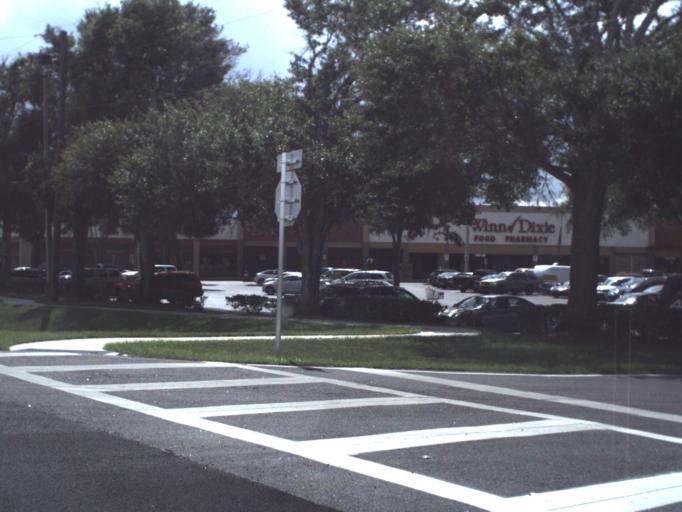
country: US
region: Florida
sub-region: Hillsborough County
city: Thonotosassa
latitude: 28.0531
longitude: -82.3333
